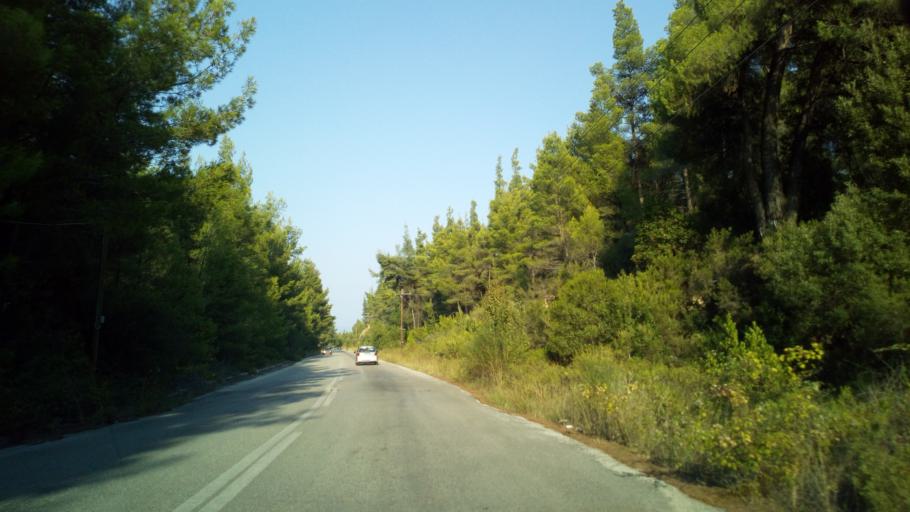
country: GR
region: Central Macedonia
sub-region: Nomos Chalkidikis
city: Neos Marmaras
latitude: 40.1791
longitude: 23.8185
